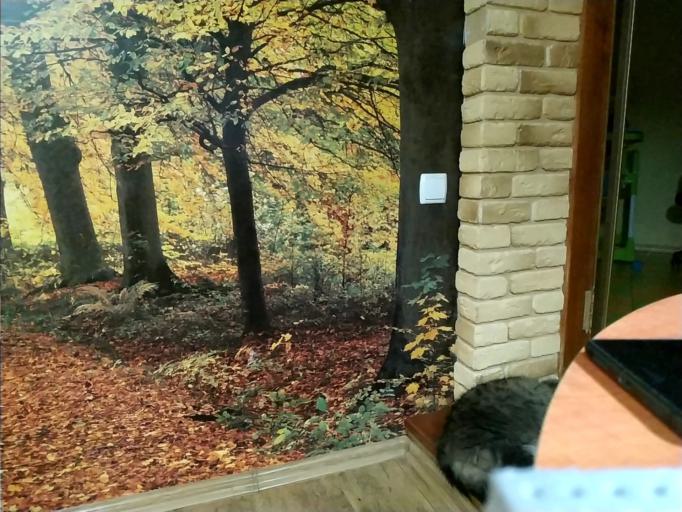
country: RU
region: Tverskaya
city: Zubtsov
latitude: 56.2730
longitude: 34.6932
